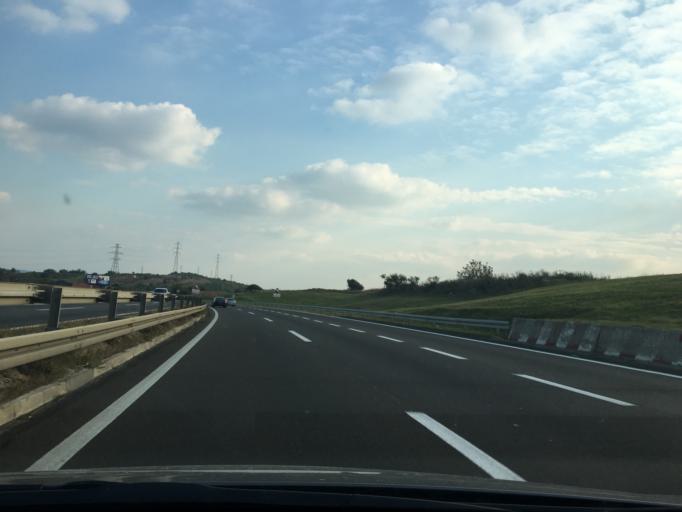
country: RS
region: Central Serbia
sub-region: Belgrade
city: Zvezdara
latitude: 44.7562
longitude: 20.5359
